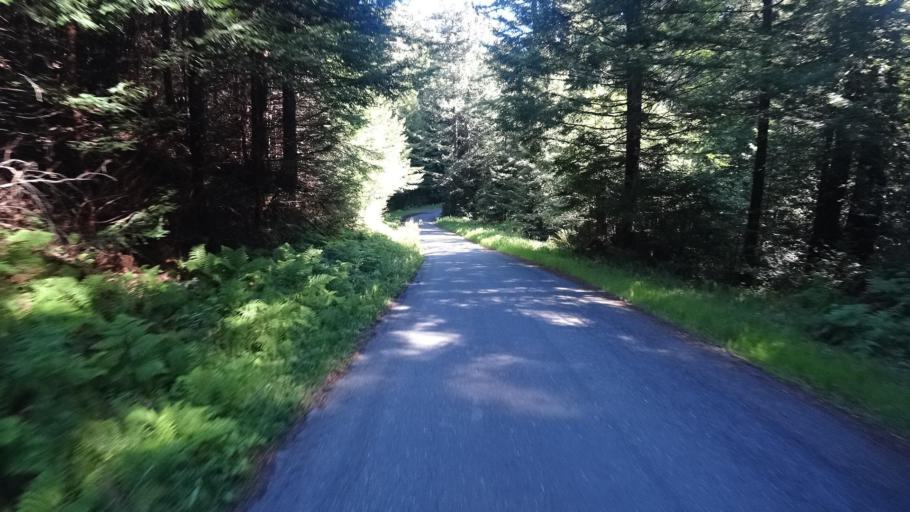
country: US
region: California
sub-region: Humboldt County
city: Rio Dell
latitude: 40.4601
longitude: -124.0008
